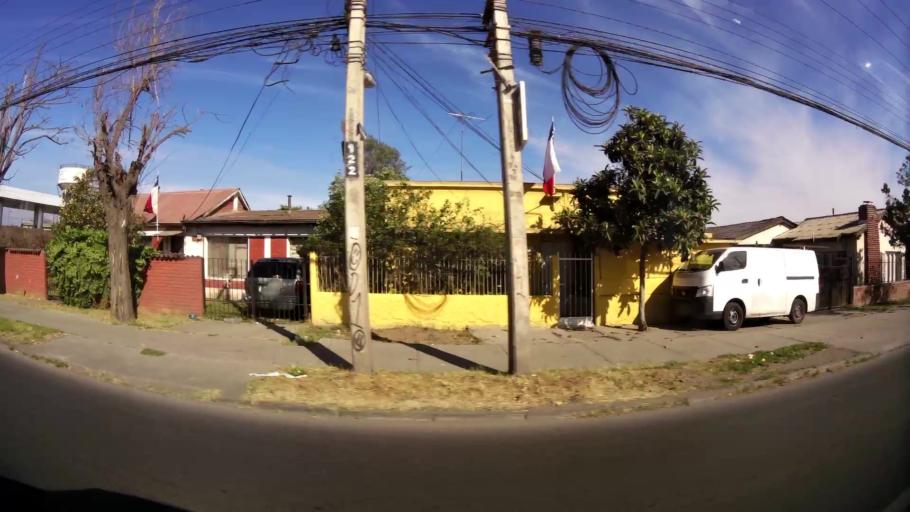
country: CL
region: Santiago Metropolitan
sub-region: Provincia de Santiago
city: Lo Prado
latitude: -33.4626
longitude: -70.6998
